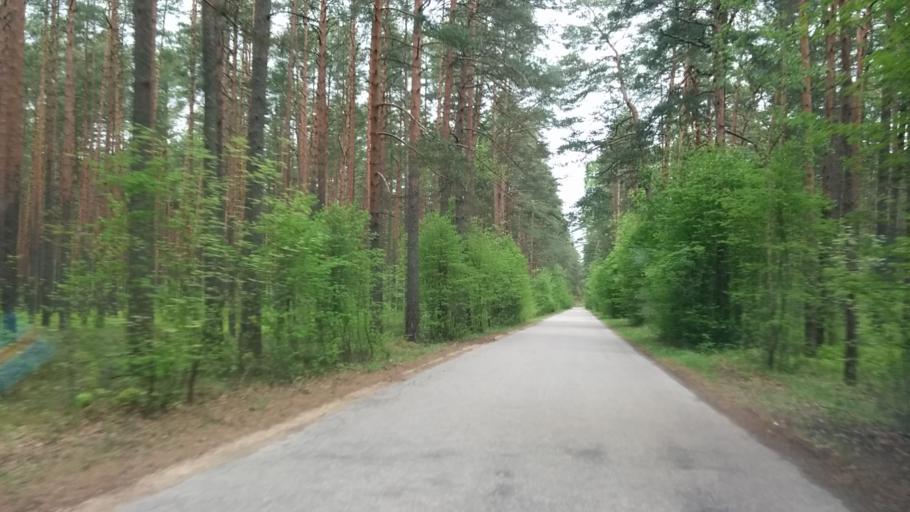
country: LV
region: Babite
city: Pinki
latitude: 56.9369
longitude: 23.9334
